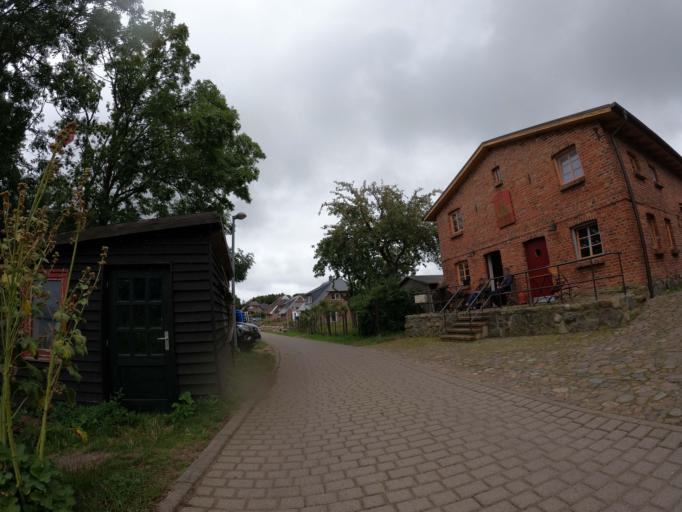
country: DE
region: Mecklenburg-Vorpommern
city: Ostseebad Sellin
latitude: 54.3054
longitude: 13.6686
